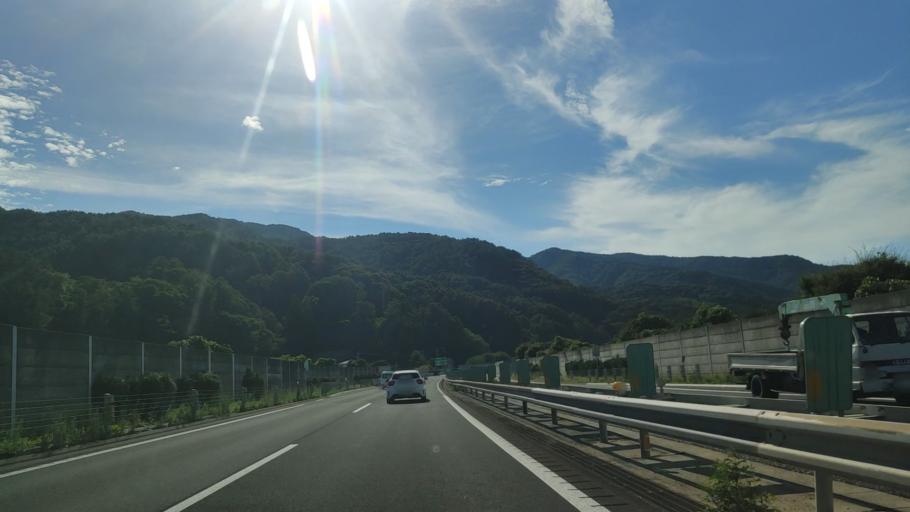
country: JP
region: Nagano
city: Suwa
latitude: 36.0028
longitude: 138.1161
